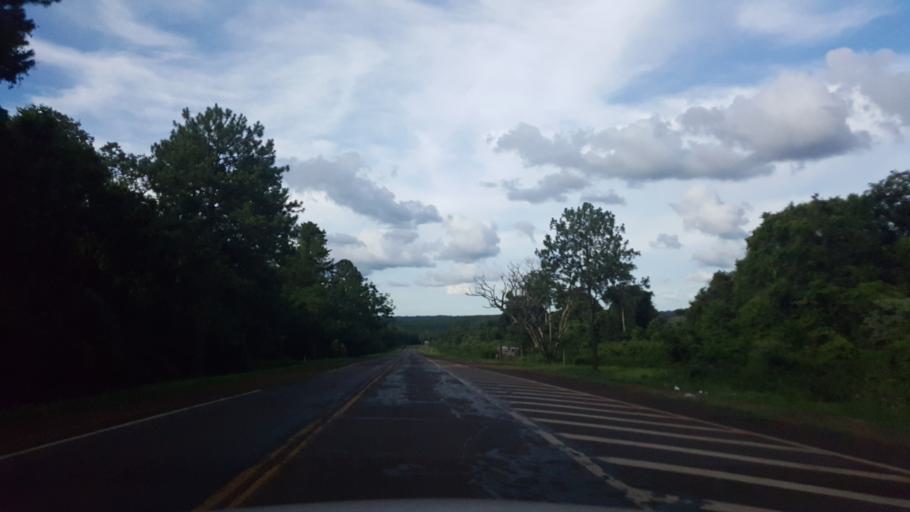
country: AR
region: Misiones
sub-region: Departamento de San Ignacio
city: San Ignacio
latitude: -27.2407
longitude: -55.5190
